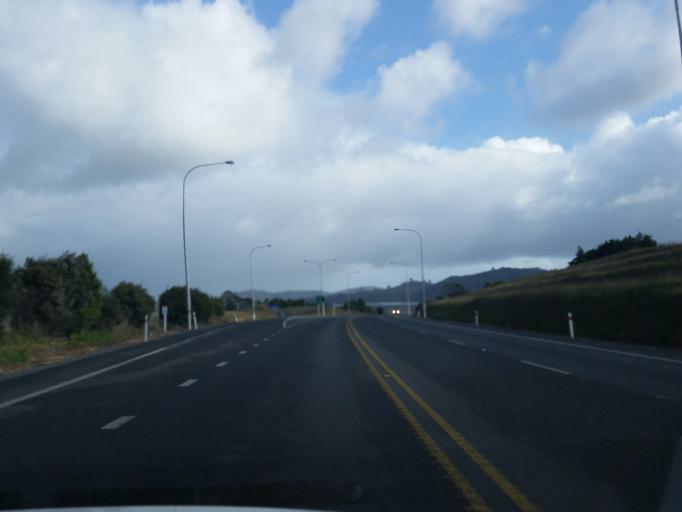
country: NZ
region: Auckland
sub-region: Auckland
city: Pukekohe East
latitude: -37.2205
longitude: 175.1188
